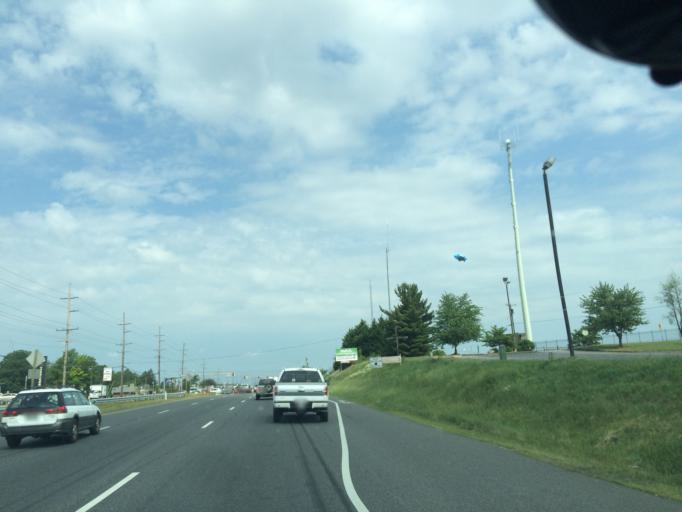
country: US
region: Maryland
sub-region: Carroll County
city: Westminster
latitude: 39.5596
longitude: -76.9660
